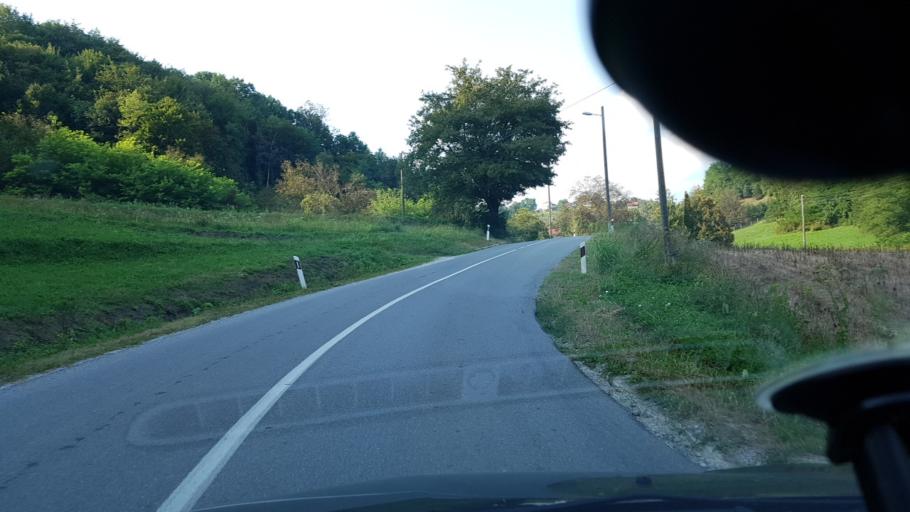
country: SI
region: Bistrica ob Sotli
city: Bistrica ob Sotli
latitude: 46.0549
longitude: 15.7708
